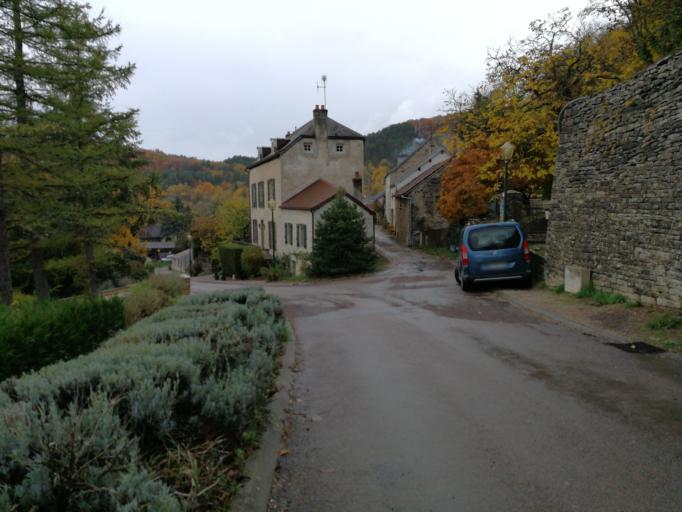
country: FR
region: Bourgogne
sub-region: Departement de la Cote-d'Or
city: Fleurey-sur-Ouche
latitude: 47.3263
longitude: 4.7902
